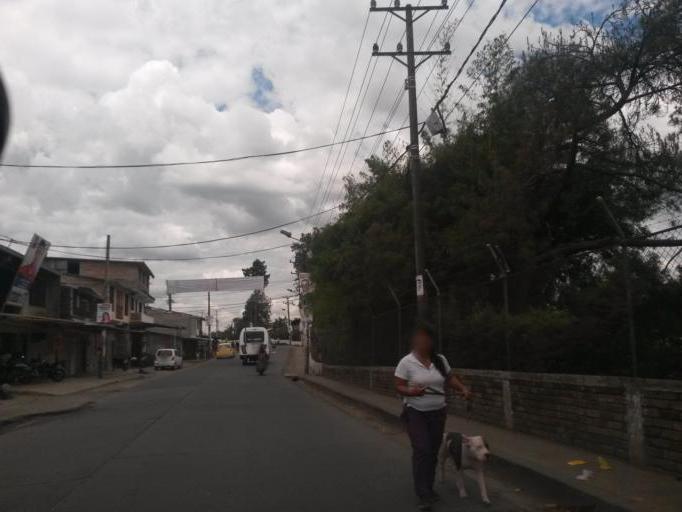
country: CO
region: Cauca
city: Popayan
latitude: 2.4497
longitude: -76.6309
